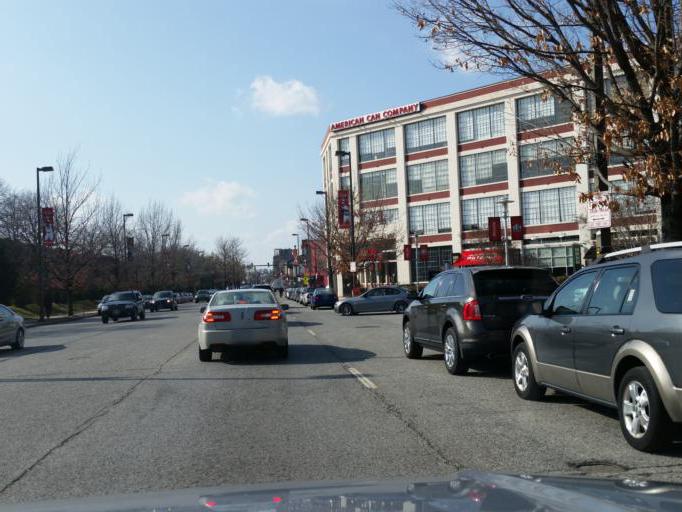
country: US
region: Maryland
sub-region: City of Baltimore
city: Baltimore
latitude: 39.2810
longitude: -76.5811
